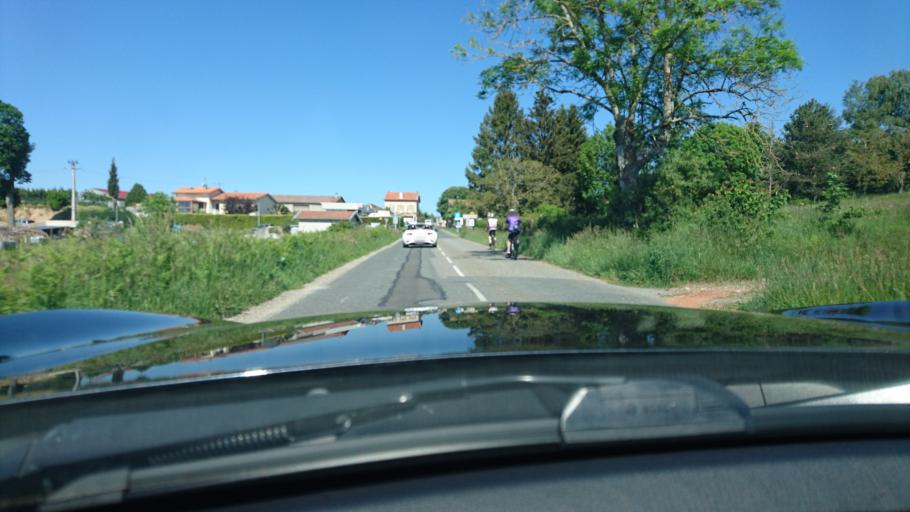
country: FR
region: Rhone-Alpes
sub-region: Departement du Rhone
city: Montrottier
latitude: 45.8093
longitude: 4.4129
